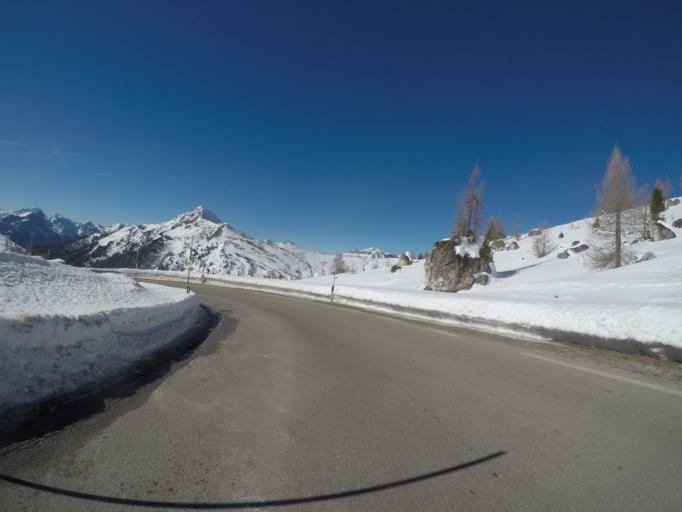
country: IT
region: Veneto
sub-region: Provincia di Belluno
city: Selva di Cadore
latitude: 46.4871
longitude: 12.0432
